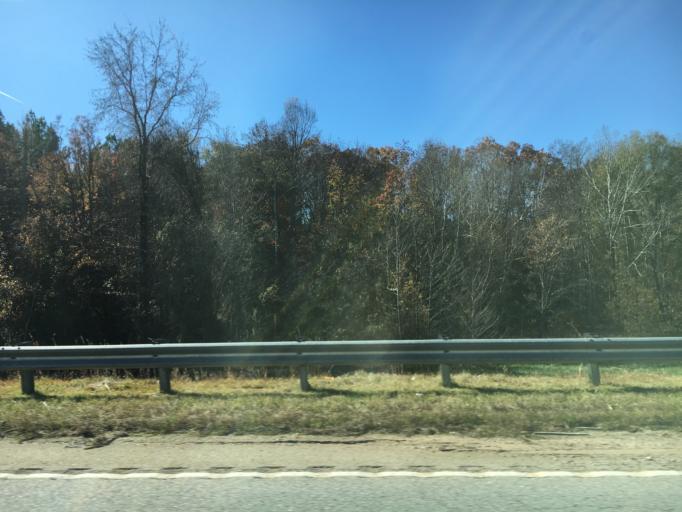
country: US
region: South Carolina
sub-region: Spartanburg County
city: Roebuck
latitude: 34.8643
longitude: -82.0265
